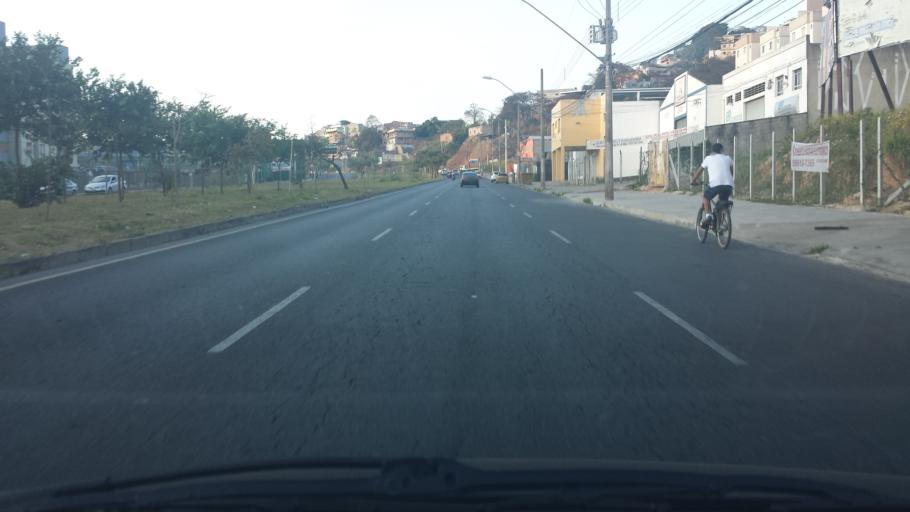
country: BR
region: Minas Gerais
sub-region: Belo Horizonte
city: Belo Horizonte
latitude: -19.8913
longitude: -43.9934
